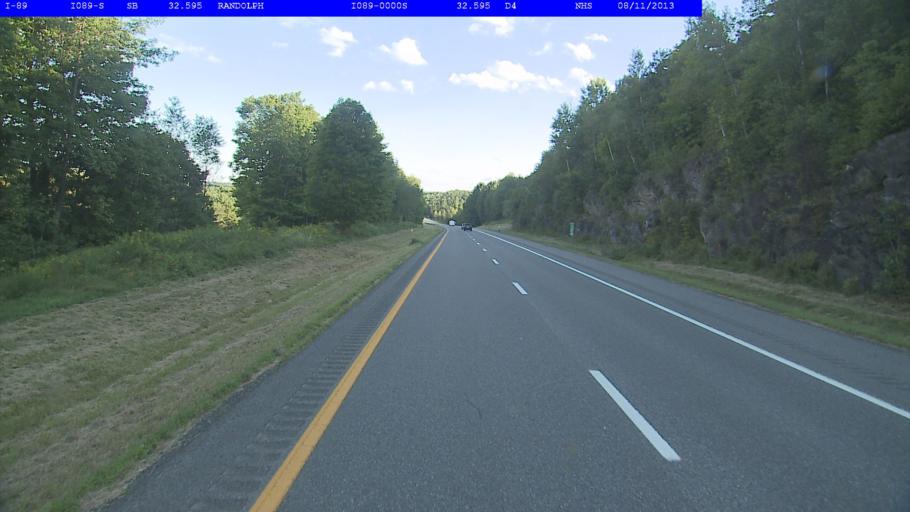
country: US
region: Vermont
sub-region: Orange County
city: Randolph
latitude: 43.9694
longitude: -72.6260
